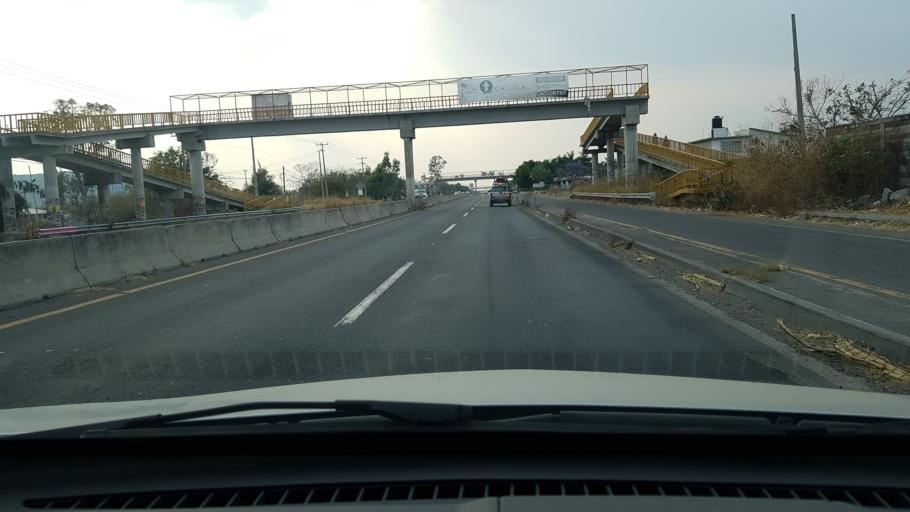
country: MX
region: Morelos
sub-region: Ayala
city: Unidad Habitacional Mariano Matamoros
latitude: 18.7453
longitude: -98.8403
